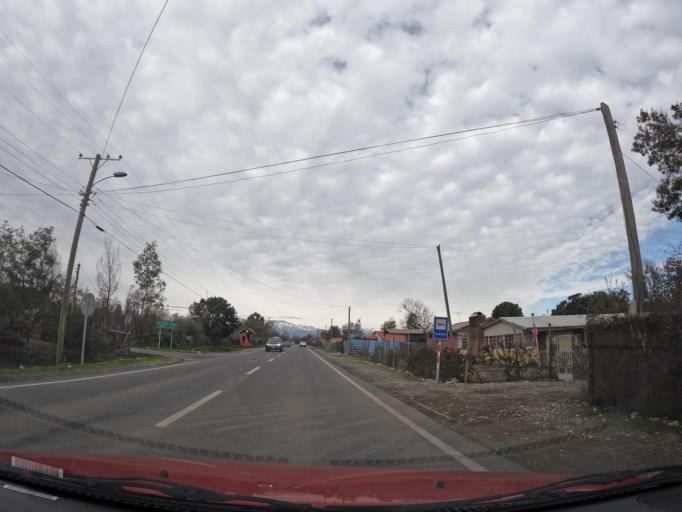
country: CL
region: Maule
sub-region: Provincia de Linares
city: Linares
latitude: -35.8840
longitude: -71.5365
